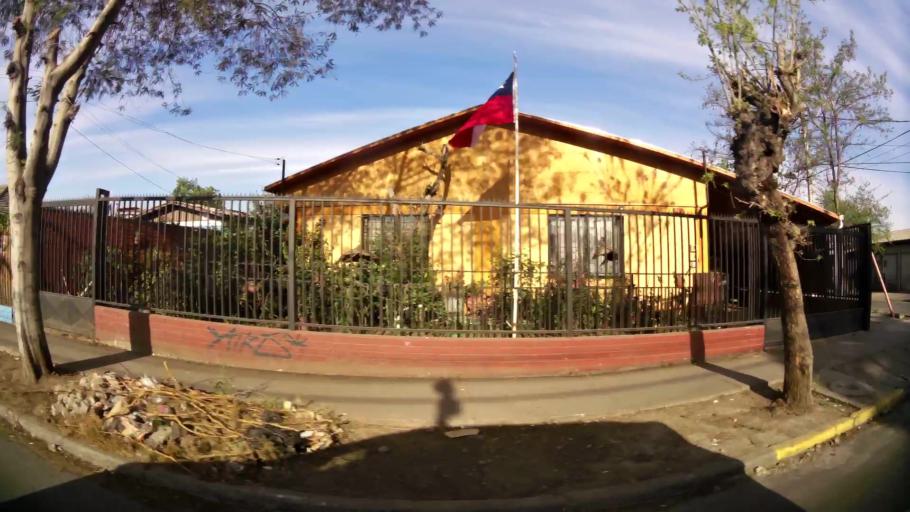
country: CL
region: Santiago Metropolitan
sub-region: Provincia de Santiago
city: Lo Prado
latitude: -33.4715
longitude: -70.6989
